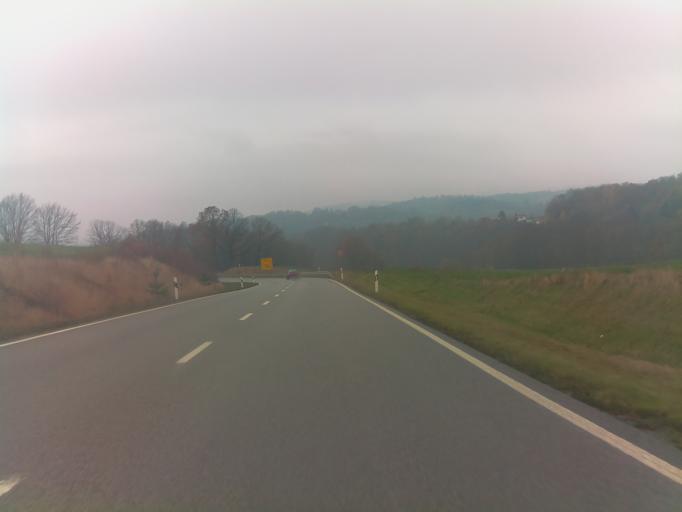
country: DE
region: Thuringia
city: Schleusingen
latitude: 50.4973
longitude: 10.7618
